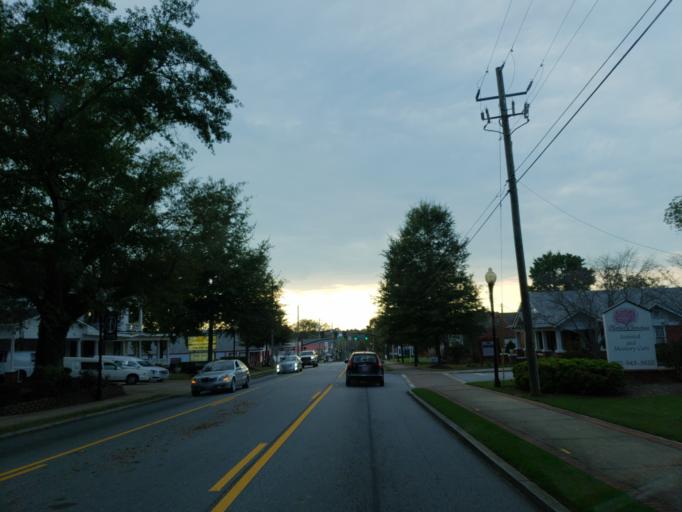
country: US
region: Georgia
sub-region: Cobb County
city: Powder Springs
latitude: 33.8596
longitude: -84.6821
